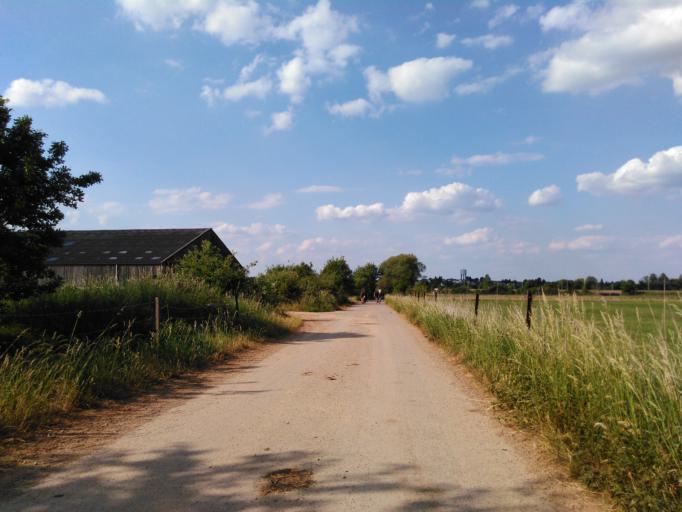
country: LU
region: Luxembourg
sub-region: Canton d'Esch-sur-Alzette
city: Kayl
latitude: 49.4977
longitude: 6.0464
